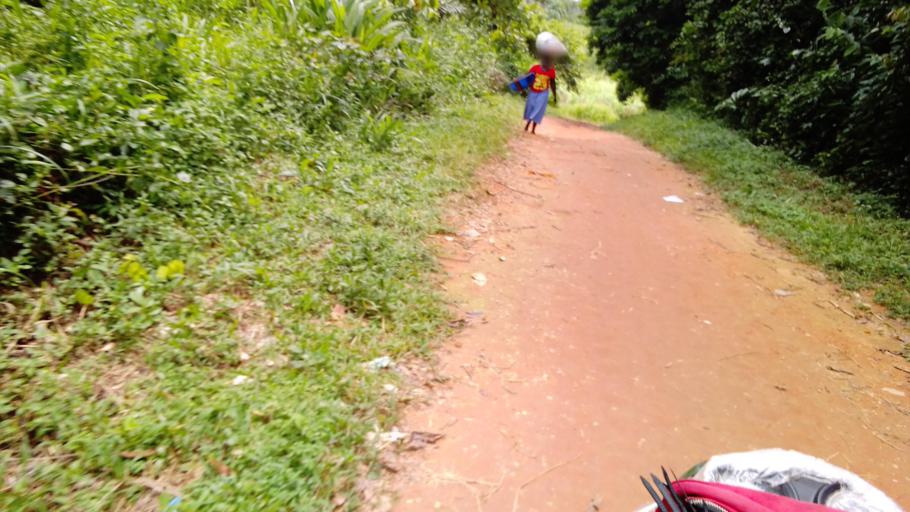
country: SL
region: Eastern Province
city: Koyima
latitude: 8.6800
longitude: -11.0067
